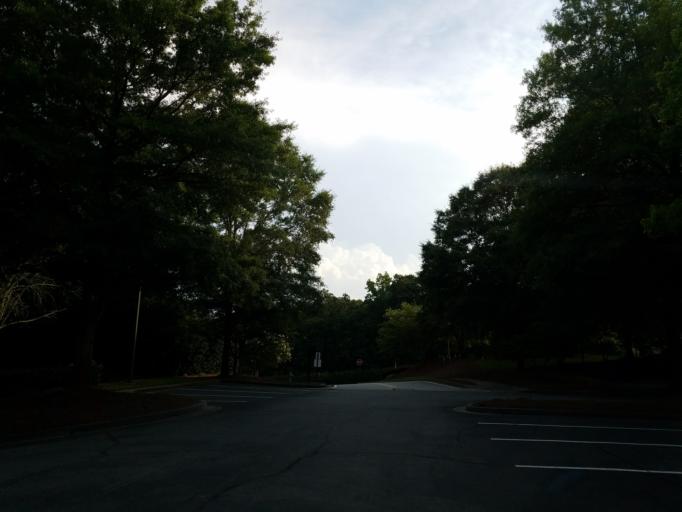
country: US
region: Georgia
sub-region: Cobb County
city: Vinings
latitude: 33.9123
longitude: -84.4589
